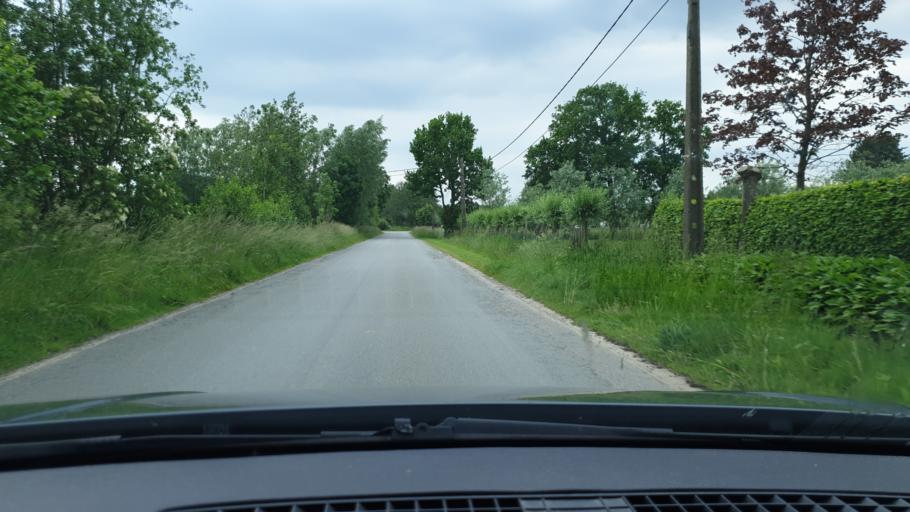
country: BE
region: Flanders
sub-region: Provincie Antwerpen
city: Geel
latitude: 51.1286
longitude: 4.9794
